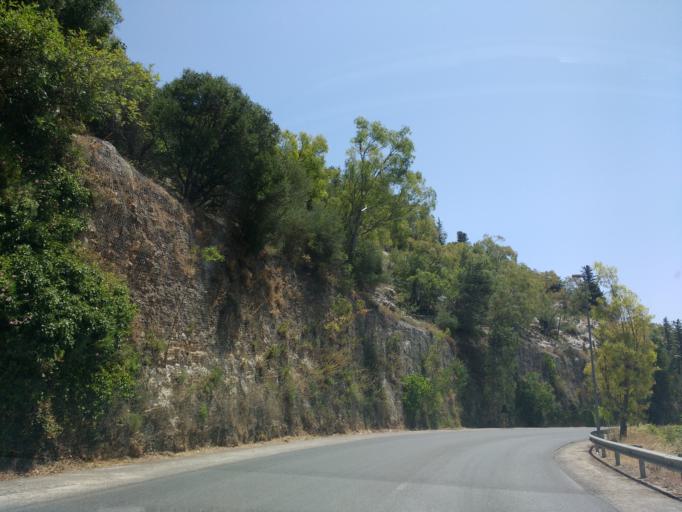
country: IT
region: Sicily
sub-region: Ragusa
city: Modica
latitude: 36.8713
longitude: 14.7506
